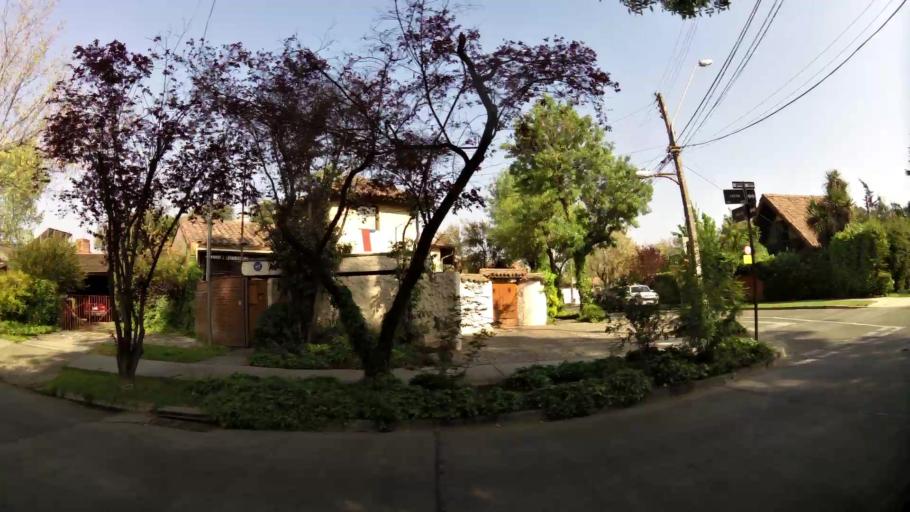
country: CL
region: Santiago Metropolitan
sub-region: Provincia de Santiago
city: Villa Presidente Frei, Nunoa, Santiago, Chile
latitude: -33.3829
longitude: -70.5637
